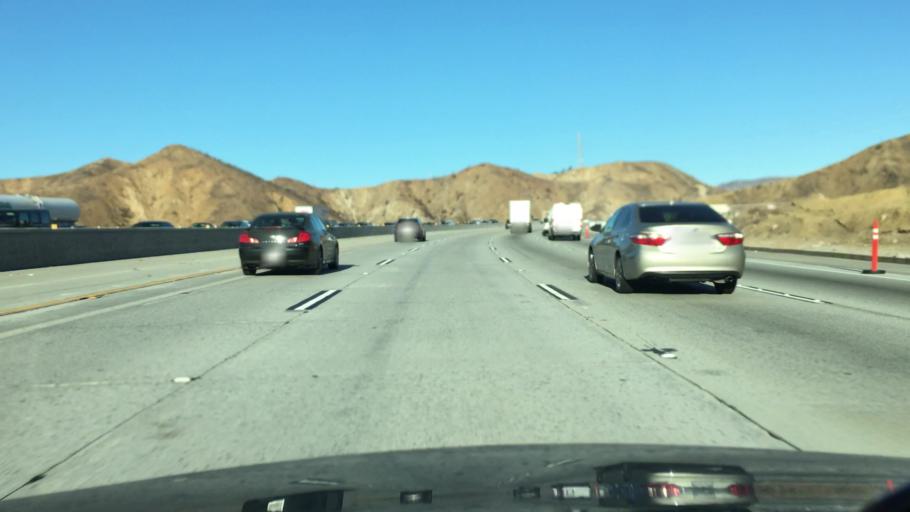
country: US
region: California
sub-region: Los Angeles County
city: Burbank
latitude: 34.2441
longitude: -118.3187
